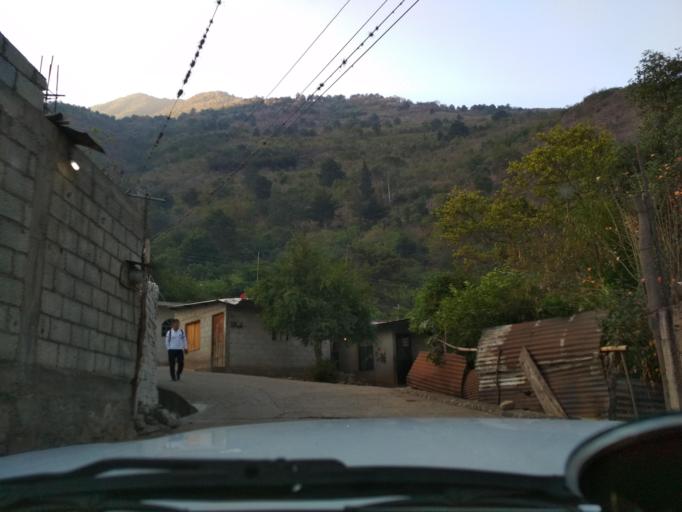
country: MX
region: Veracruz
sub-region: Nogales
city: Taza de Agua Ojo Zarco
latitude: 18.7713
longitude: -97.1944
